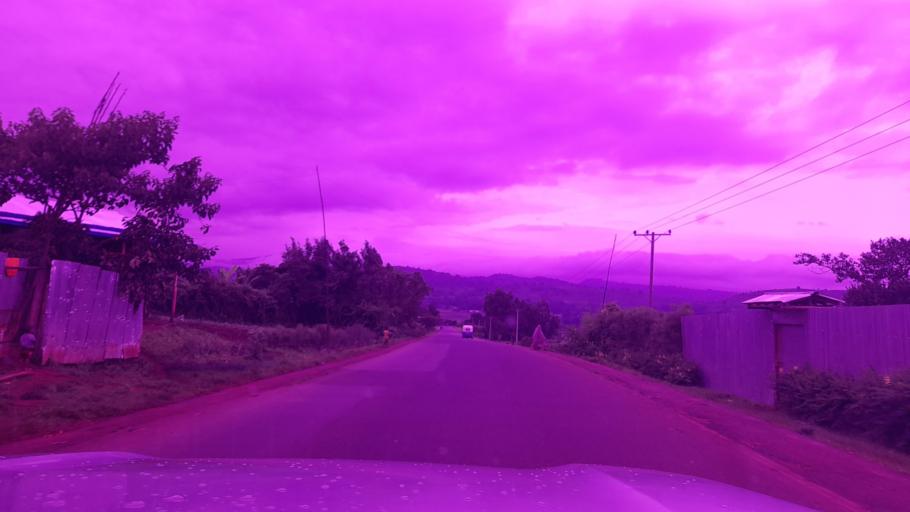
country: ET
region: Oromiya
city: Jima
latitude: 7.7482
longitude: 37.3230
